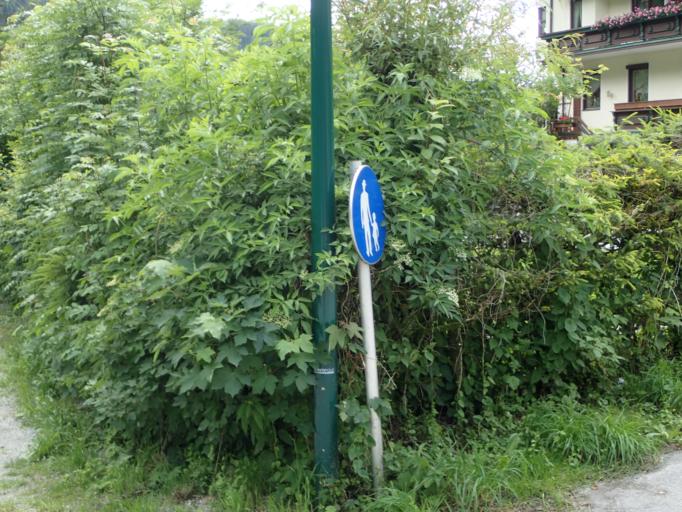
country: AT
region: Salzburg
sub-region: Politischer Bezirk Sankt Johann im Pongau
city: Wagrain
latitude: 47.3360
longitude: 13.3030
